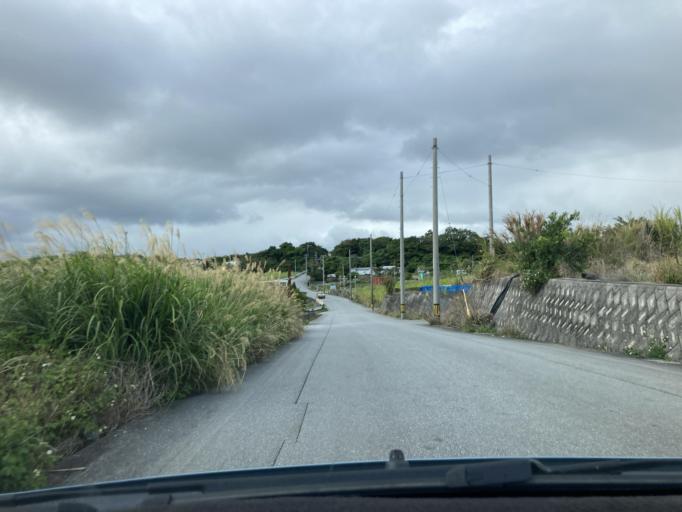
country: JP
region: Okinawa
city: Itoman
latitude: 26.1272
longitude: 127.6865
